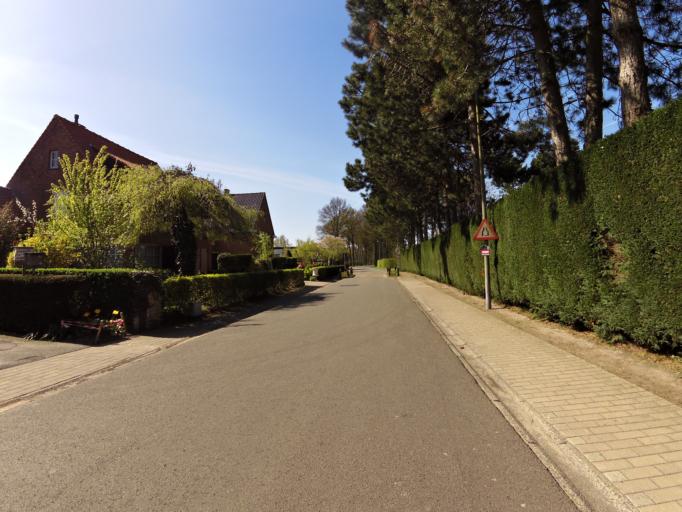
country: BE
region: Flanders
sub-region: Provincie West-Vlaanderen
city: Jabbeke
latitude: 51.1842
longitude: 3.0904
